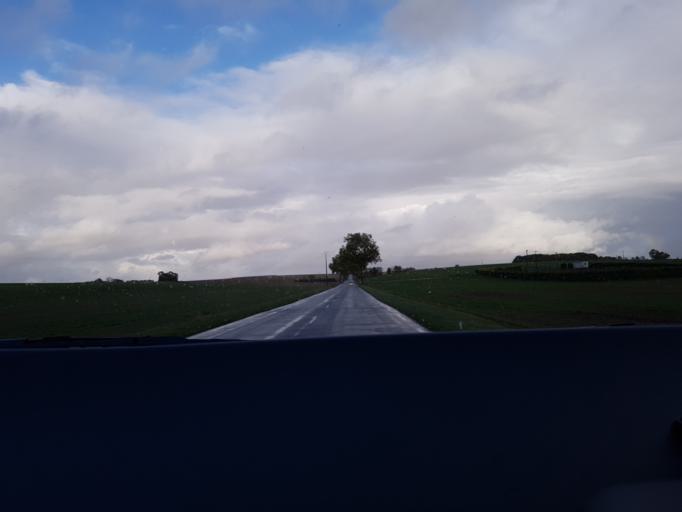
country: FR
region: Poitou-Charentes
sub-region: Departement de la Charente-Maritime
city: Aulnay
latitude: 46.0036
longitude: -0.3922
